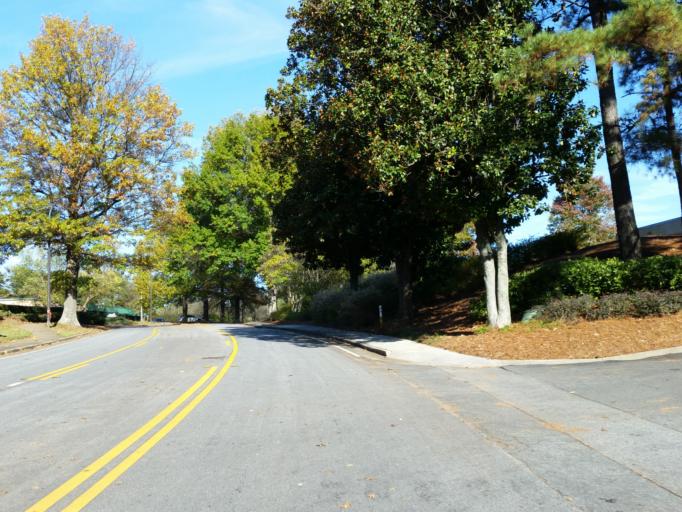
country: US
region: Georgia
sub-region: Cobb County
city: Vinings
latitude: 33.9033
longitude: -84.4654
